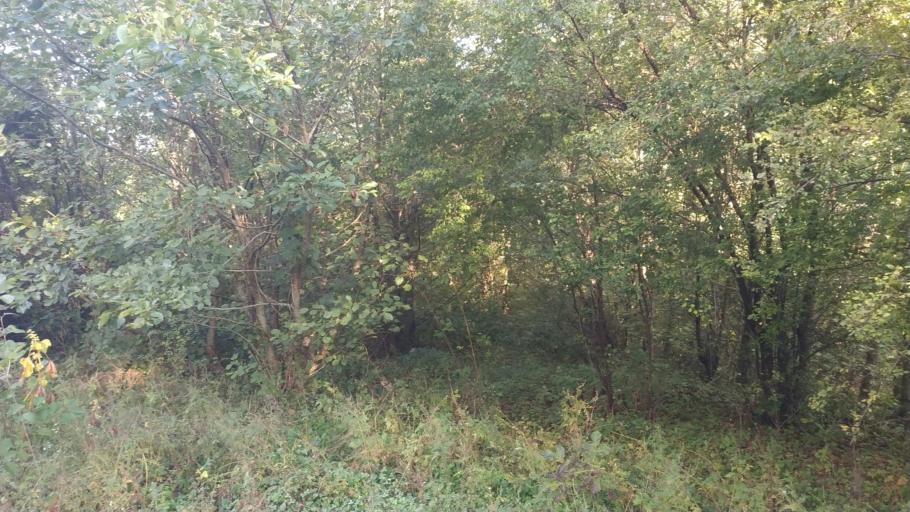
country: RU
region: Krasnodarskiy
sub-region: Sochi City
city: Lazarevskoye
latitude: 43.9968
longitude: 39.3736
